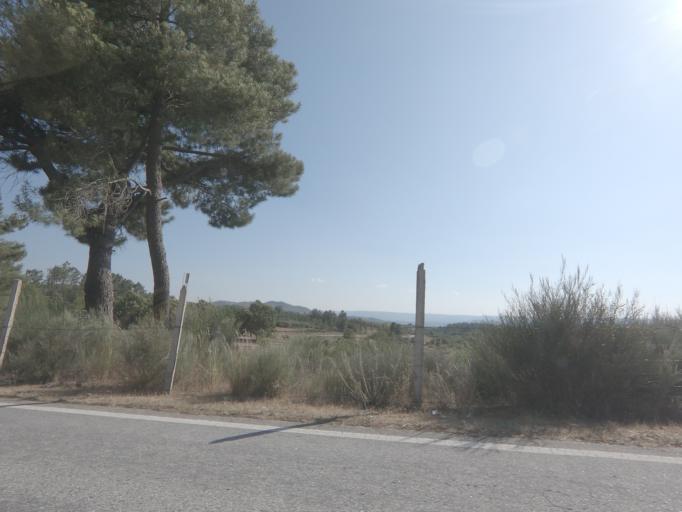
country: PT
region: Viseu
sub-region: Tabuaco
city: Tabuaco
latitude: 41.0598
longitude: -7.5612
